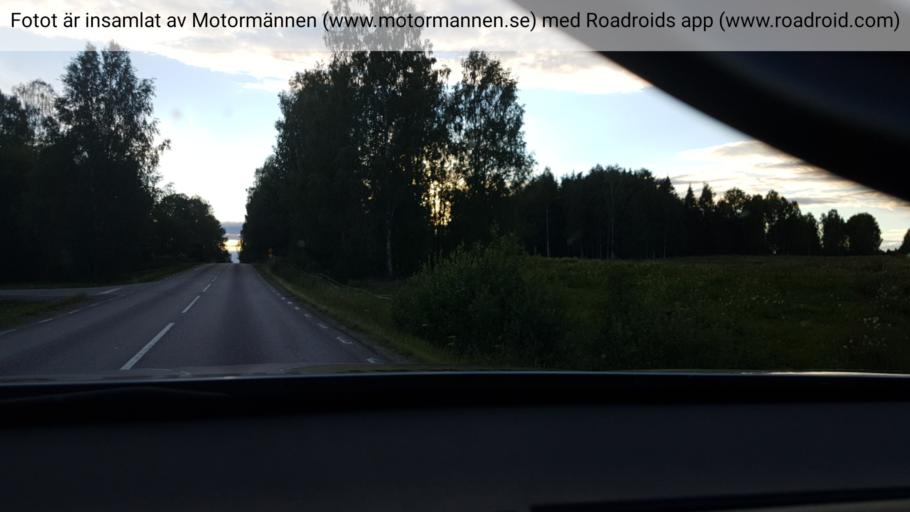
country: SE
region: Vaermland
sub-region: Torsby Kommun
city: Torsby
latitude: 60.1322
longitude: 13.0505
